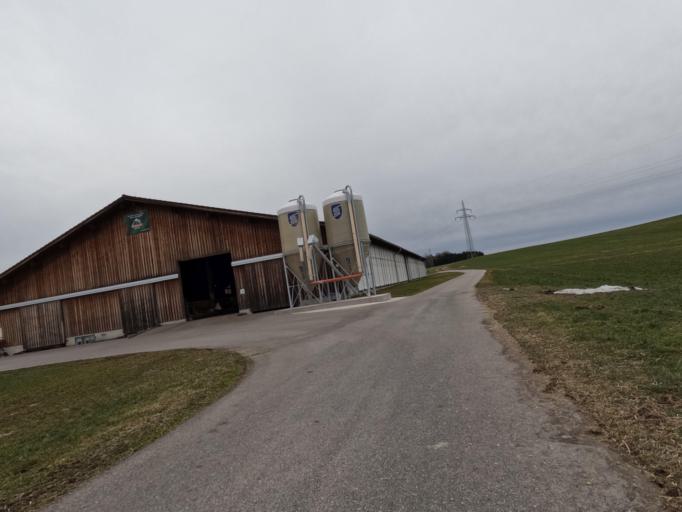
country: DE
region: Bavaria
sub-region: Upper Bavaria
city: Vachendorf
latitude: 47.8529
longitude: 12.5806
